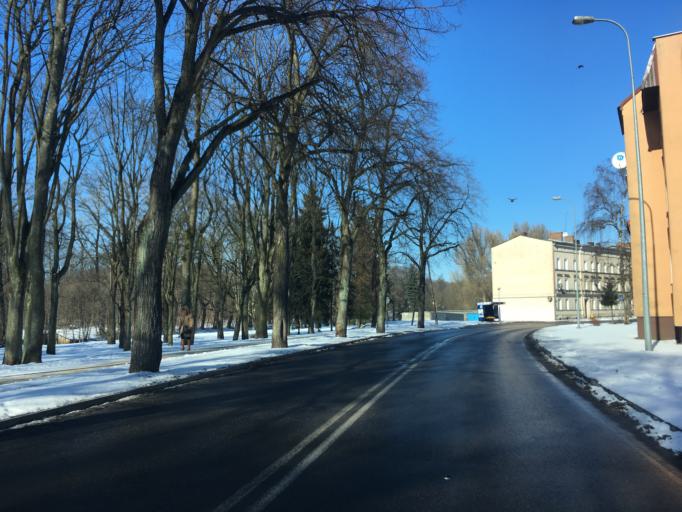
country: PL
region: Pomeranian Voivodeship
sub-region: Slupsk
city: Slupsk
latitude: 54.4602
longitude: 17.0409
